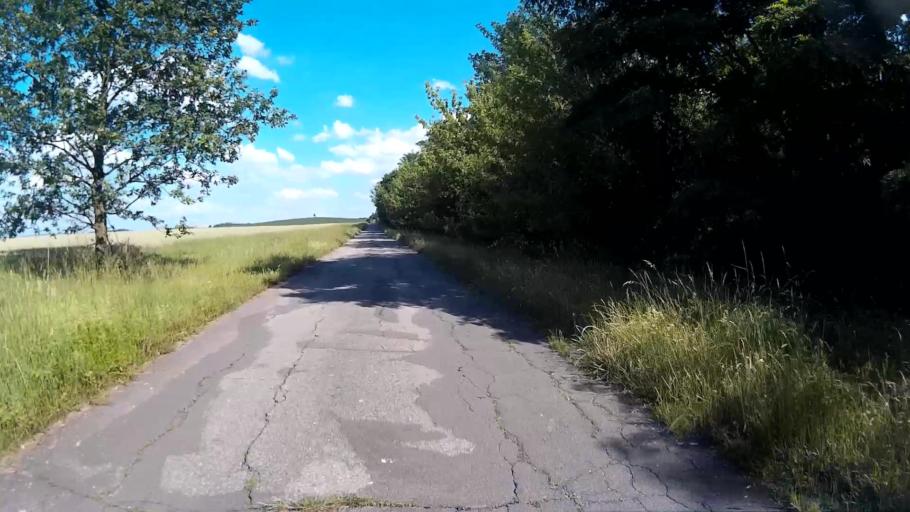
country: CZ
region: South Moravian
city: Moutnice
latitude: 49.0423
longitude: 16.7089
